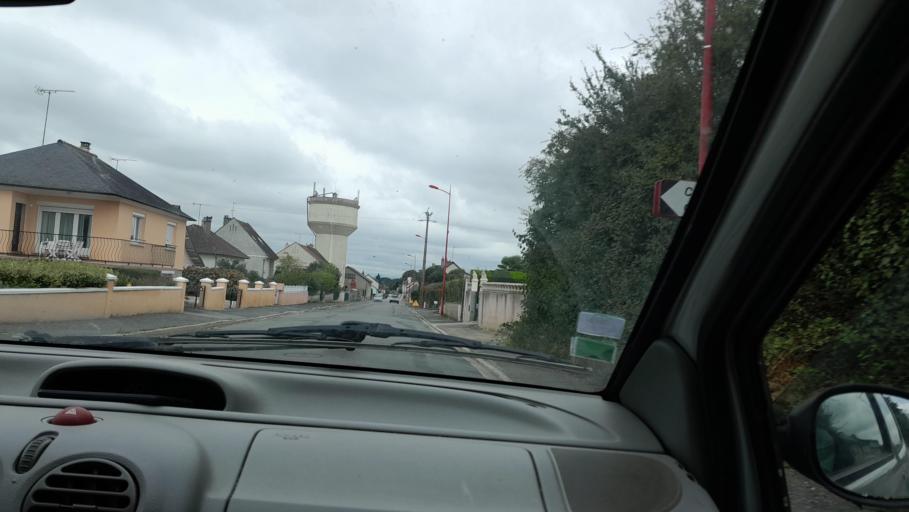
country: FR
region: Pays de la Loire
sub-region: Departement de la Mayenne
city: Cosse-le-Vivien
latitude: 47.9421
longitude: -0.9064
